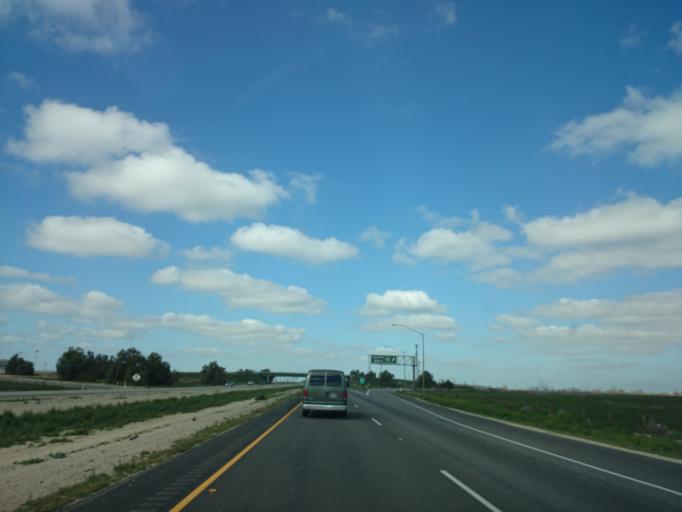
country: US
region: California
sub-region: Kern County
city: Rosedale
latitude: 35.2901
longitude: -119.2489
